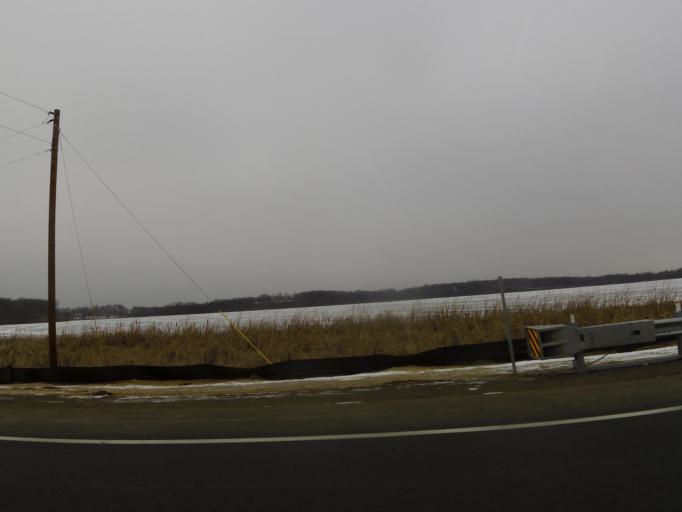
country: US
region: Minnesota
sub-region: Scott County
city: Prior Lake
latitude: 44.6275
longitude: -93.4806
